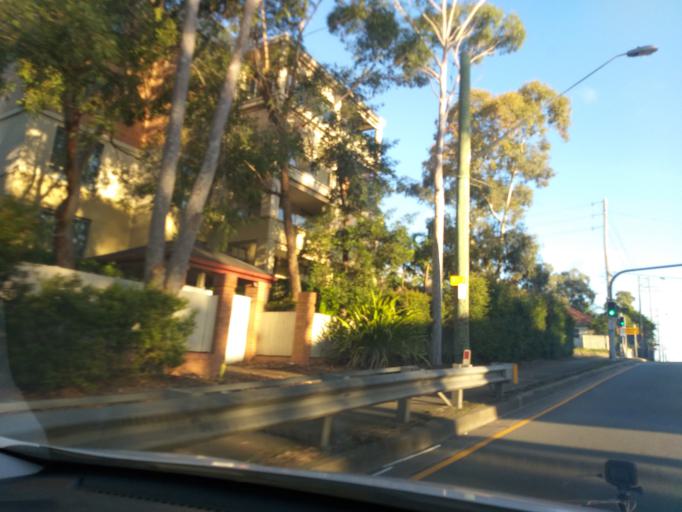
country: AU
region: New South Wales
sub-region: Sutherland Shire
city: Kirrawee
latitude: -34.0326
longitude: 151.0669
